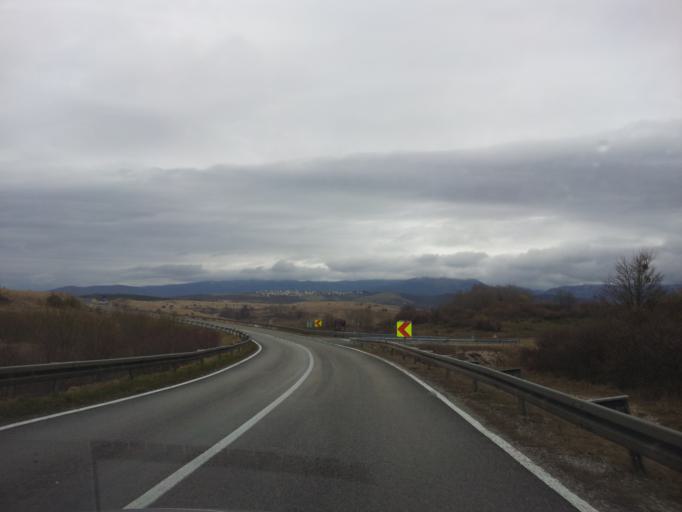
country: HR
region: Zadarska
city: Gracac
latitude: 44.4960
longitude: 15.7462
